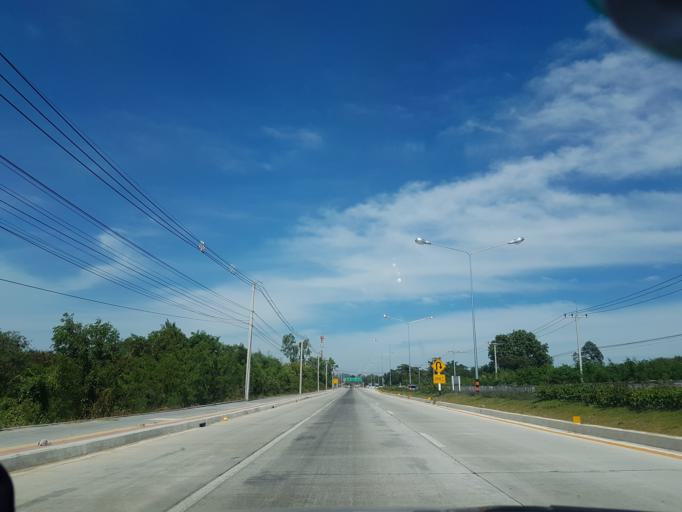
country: TH
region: Chon Buri
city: Sattahip
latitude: 12.6821
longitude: 100.9784
